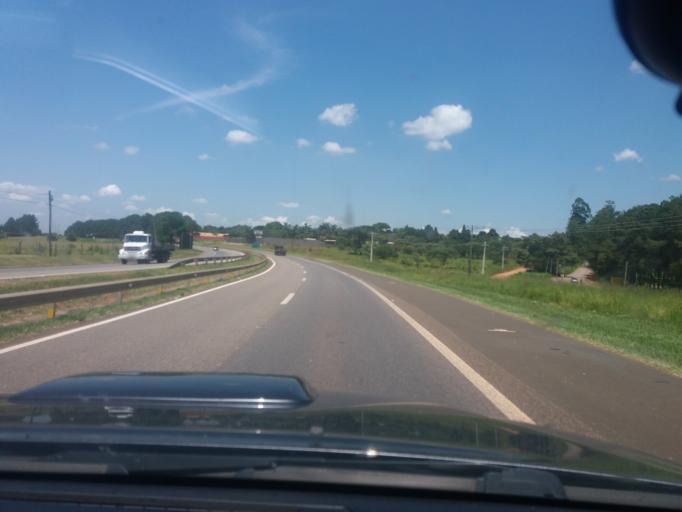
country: BR
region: Sao Paulo
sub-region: Tatui
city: Tatui
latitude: -23.3605
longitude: -47.8947
